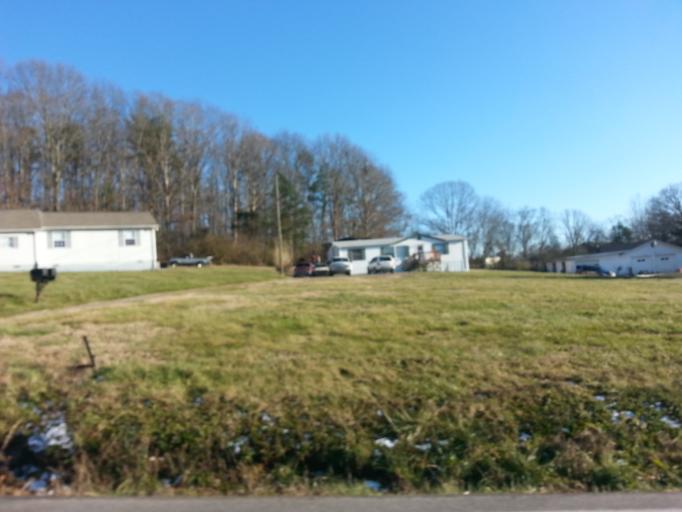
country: US
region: Tennessee
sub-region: Knox County
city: Farragut
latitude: 35.9531
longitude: -84.0623
